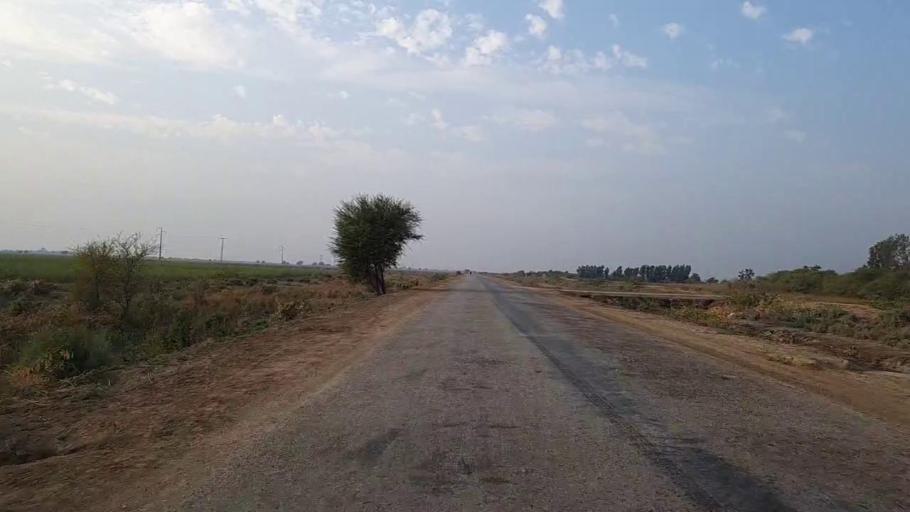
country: PK
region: Sindh
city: Pithoro
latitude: 25.4081
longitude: 69.3926
